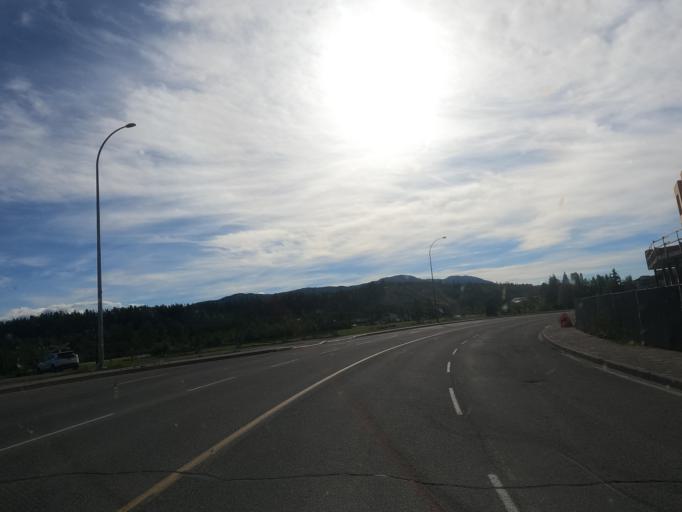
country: CA
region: Yukon
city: Whitehorse
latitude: 60.7294
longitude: -135.0604
